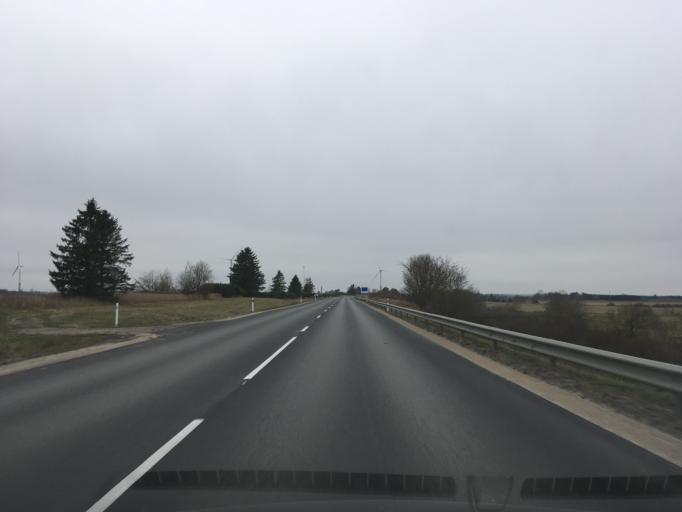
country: EE
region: Ida-Virumaa
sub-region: Aseri vald
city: Aseri
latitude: 59.4427
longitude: 26.7931
